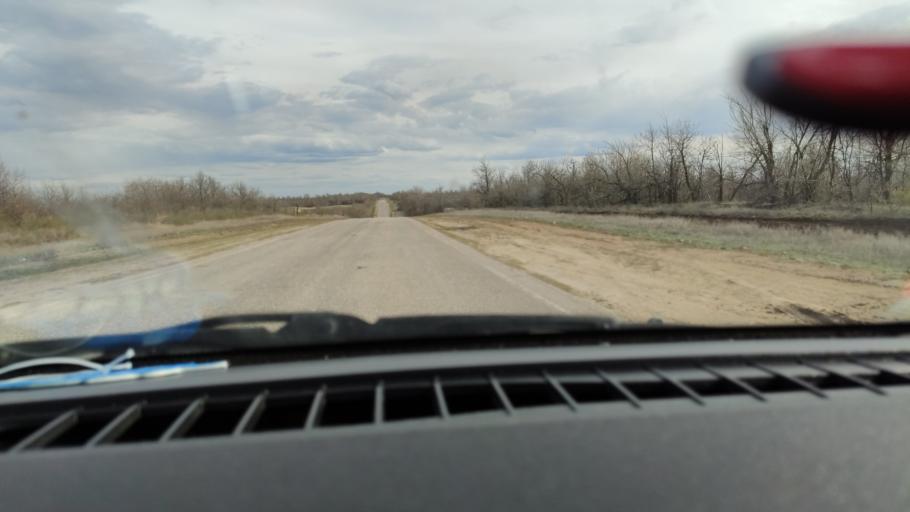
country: RU
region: Saratov
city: Rovnoye
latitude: 50.9888
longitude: 46.1111
